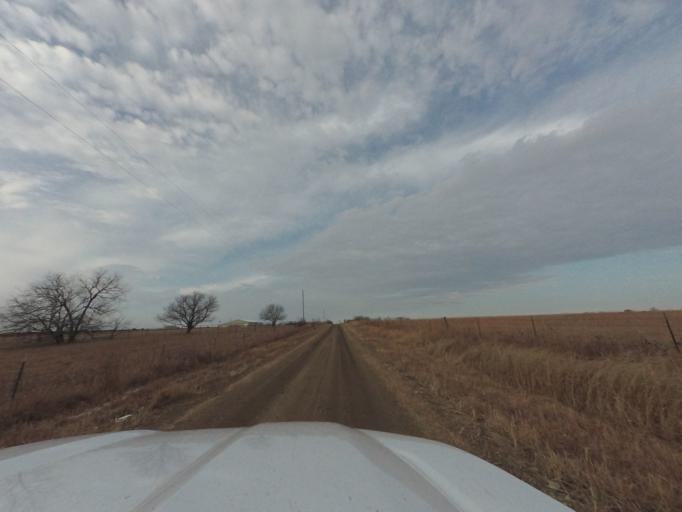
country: US
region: Kansas
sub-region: Chase County
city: Cottonwood Falls
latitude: 38.4786
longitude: -96.4270
